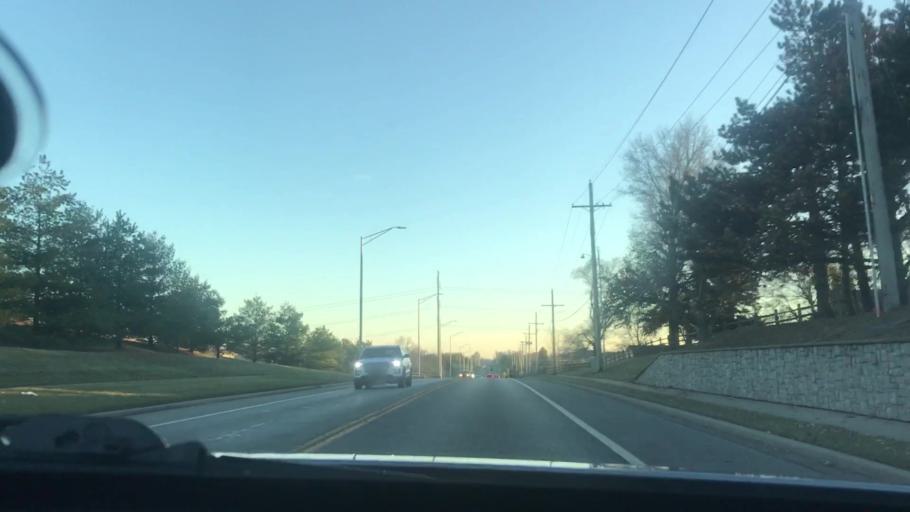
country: US
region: Kansas
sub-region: Johnson County
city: Olathe
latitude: 38.9369
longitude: -94.8161
